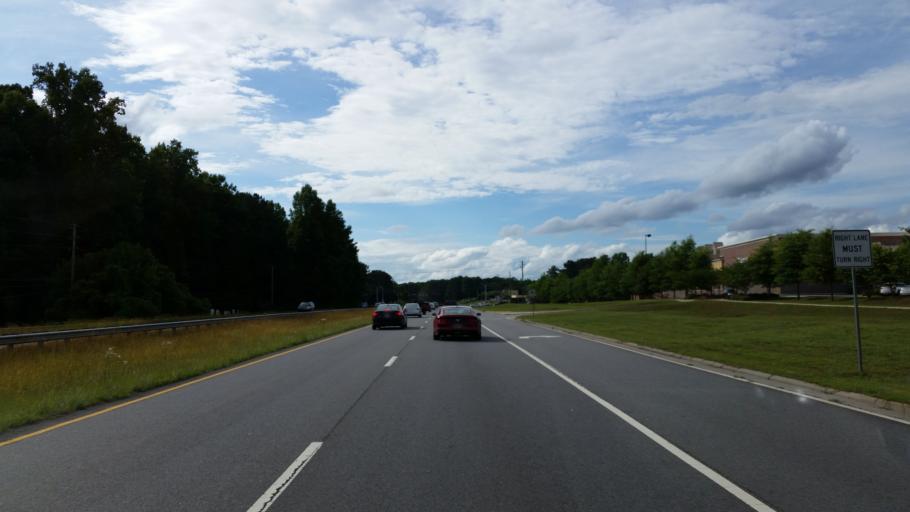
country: US
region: Georgia
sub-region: Cobb County
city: Acworth
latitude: 34.0469
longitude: -84.6983
